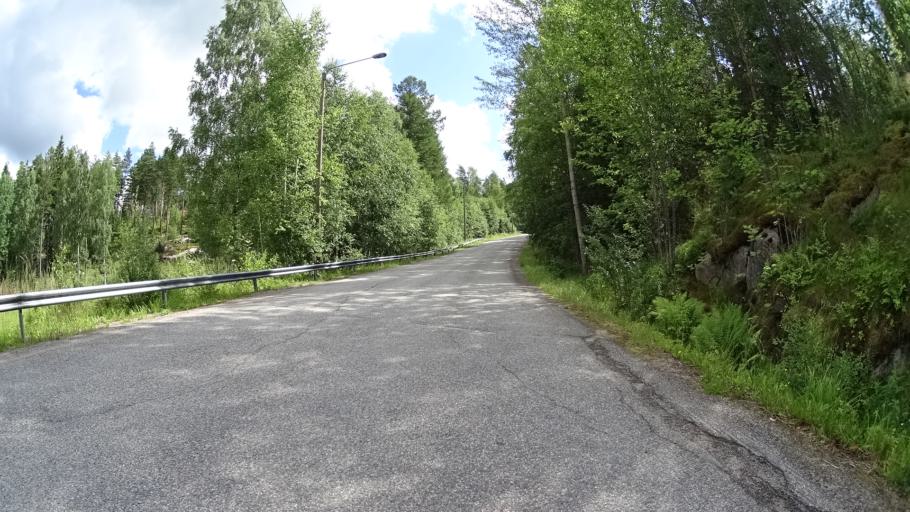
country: FI
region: Uusimaa
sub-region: Helsinki
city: Espoo
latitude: 60.3591
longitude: 24.6636
